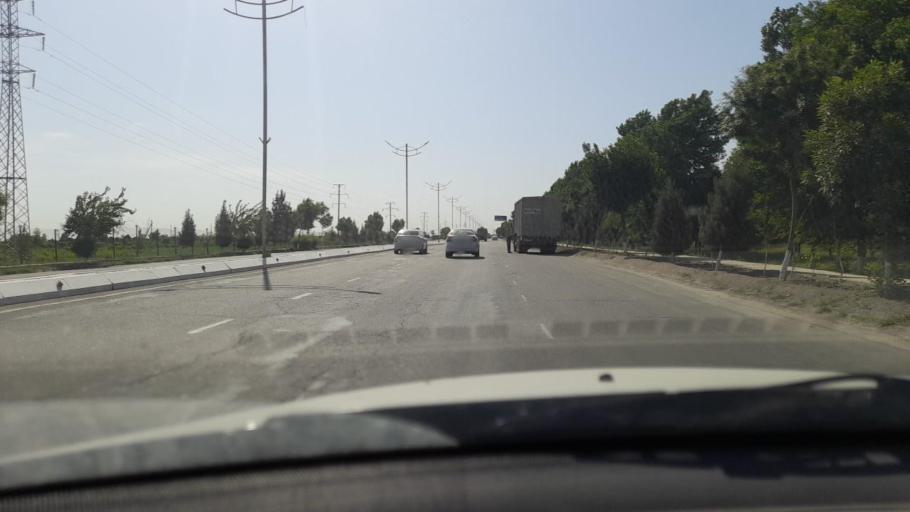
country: UZ
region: Bukhara
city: Bukhara
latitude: 39.8005
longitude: 64.4324
